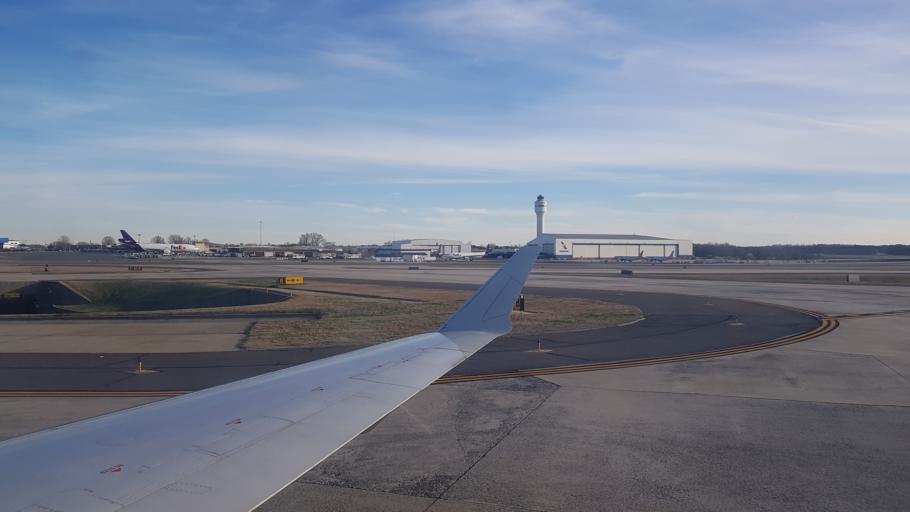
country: US
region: North Carolina
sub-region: Gaston County
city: Belmont
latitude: 35.2157
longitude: -80.9451
